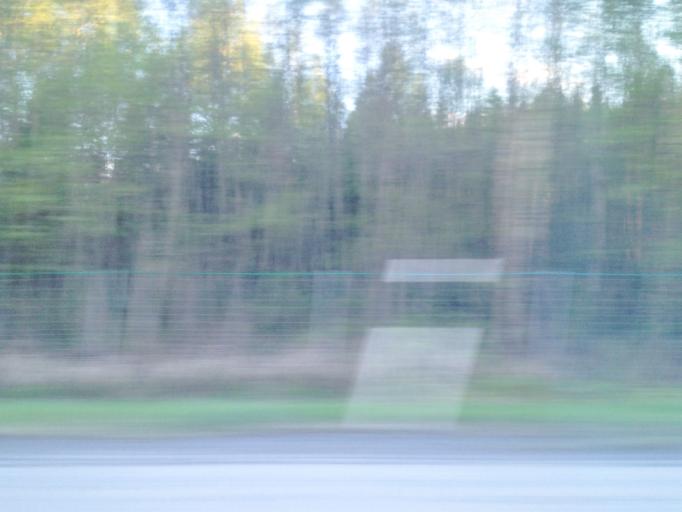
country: FI
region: Haeme
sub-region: Haemeenlinna
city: Parola
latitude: 61.0516
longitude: 24.3542
